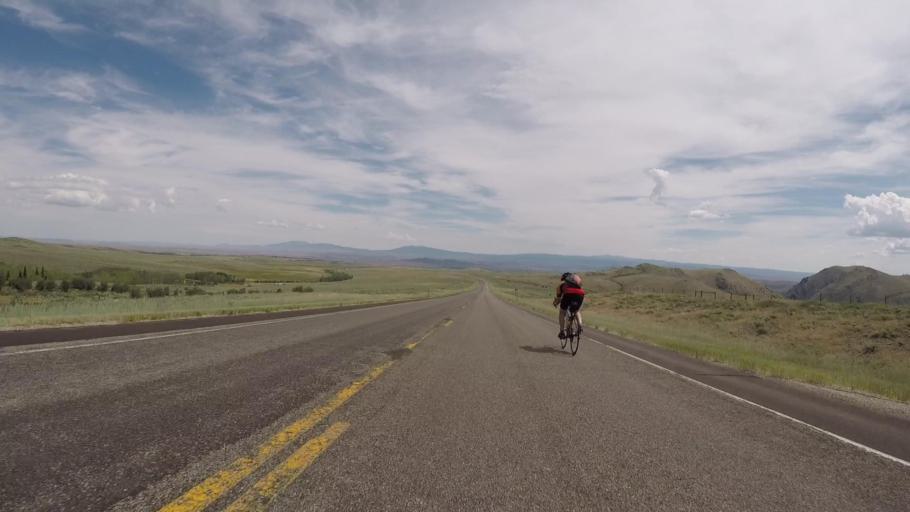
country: US
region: Wyoming
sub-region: Carbon County
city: Saratoga
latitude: 41.1839
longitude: -106.8627
